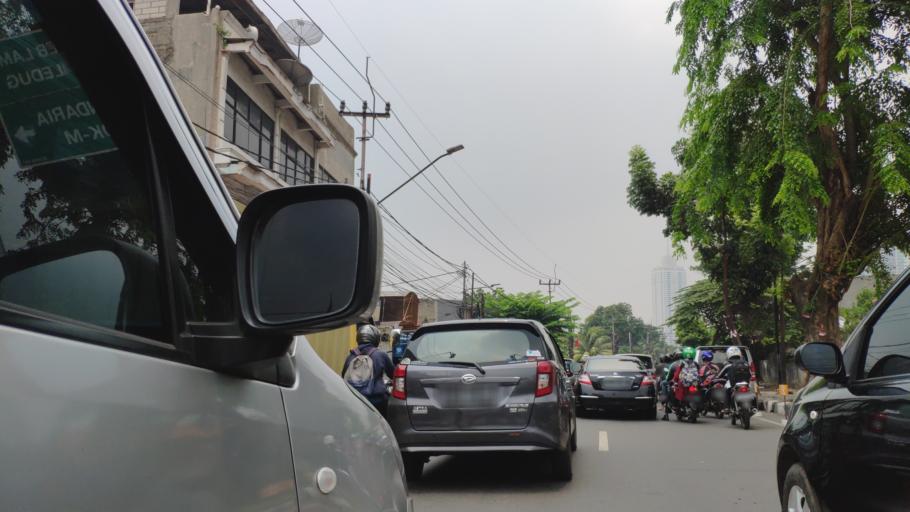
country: ID
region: Banten
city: South Tangerang
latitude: -6.2479
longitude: 106.7785
